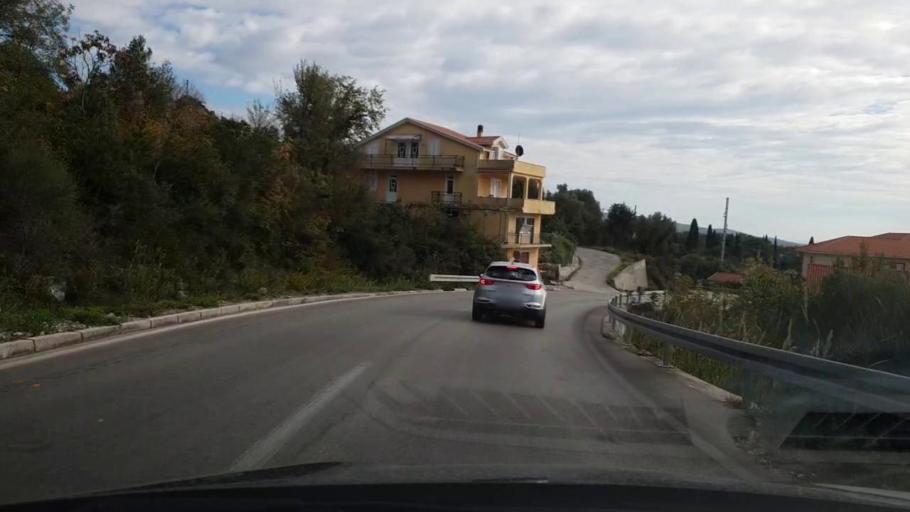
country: ME
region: Herceg Novi
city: Herceg-Novi
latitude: 42.4646
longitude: 18.5454
